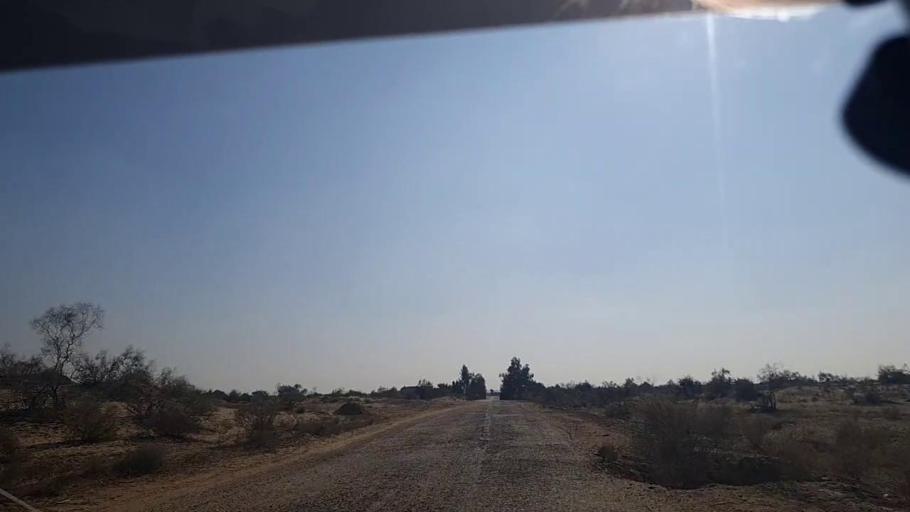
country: PK
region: Sindh
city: Khanpur
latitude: 27.5704
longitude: 69.3051
